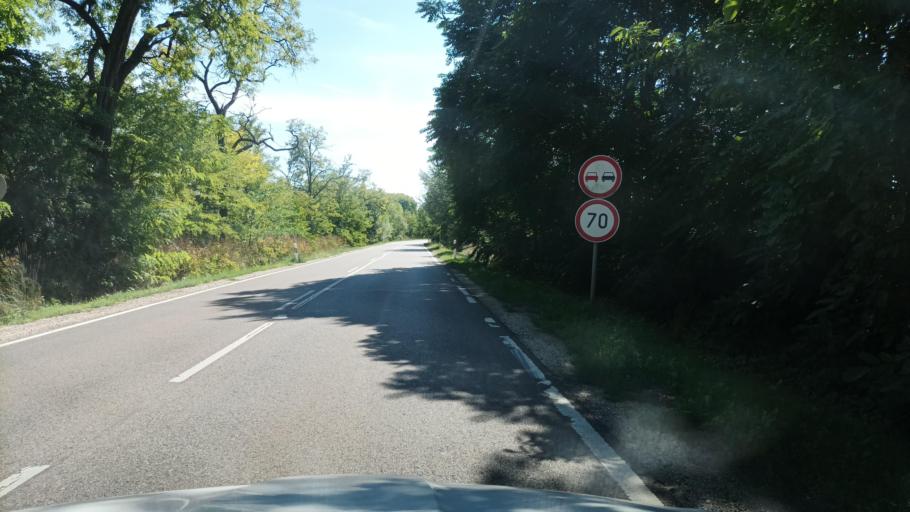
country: HU
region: Pest
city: Zsambok
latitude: 47.5379
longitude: 19.6029
